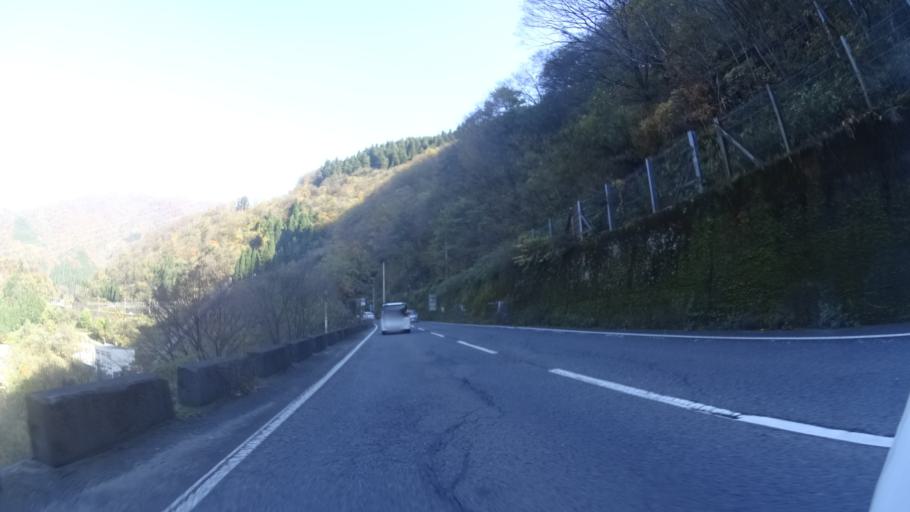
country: JP
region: Fukui
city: Ono
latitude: 35.9649
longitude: 136.5885
